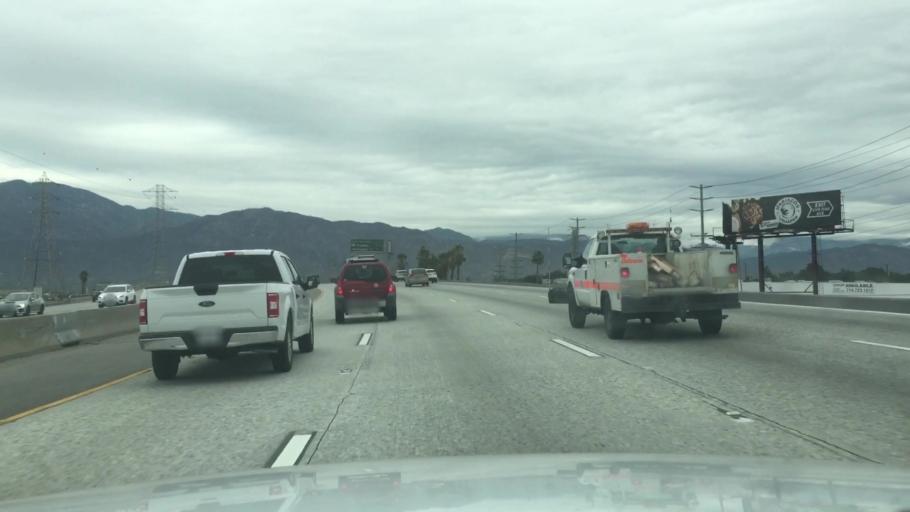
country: US
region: California
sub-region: Los Angeles County
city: Baldwin Park
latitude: 34.0965
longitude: -117.9862
